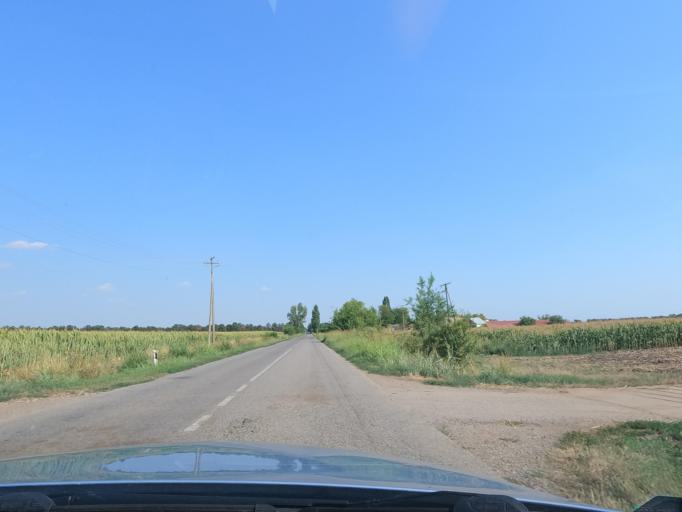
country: RS
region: Autonomna Pokrajina Vojvodina
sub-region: Juznobacki Okrug
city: Becej
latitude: 45.6342
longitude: 20.0100
